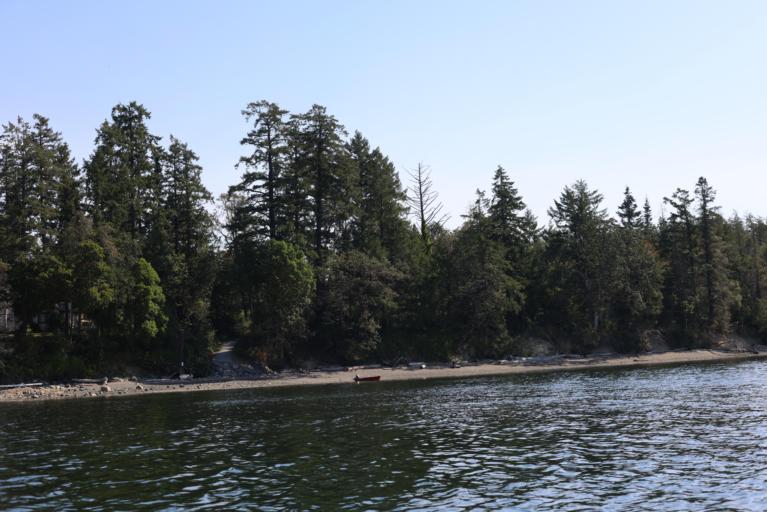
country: CA
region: British Columbia
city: North Saanich
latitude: 48.6286
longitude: -123.4677
